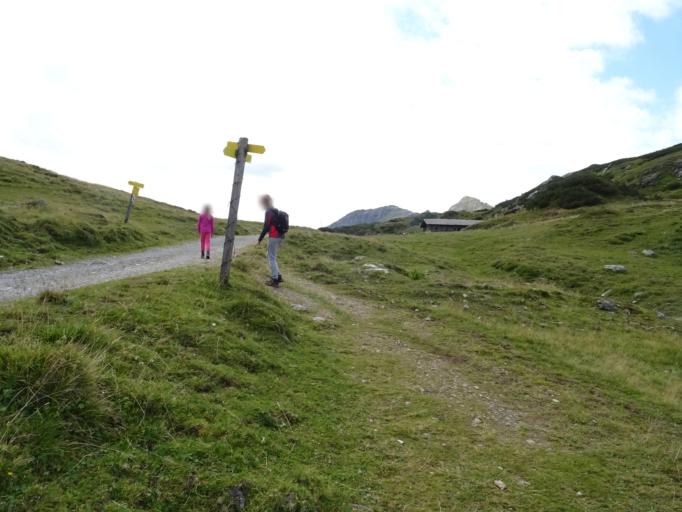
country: AT
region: Salzburg
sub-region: Politischer Bezirk Tamsweg
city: Tweng
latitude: 47.2824
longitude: 13.6007
